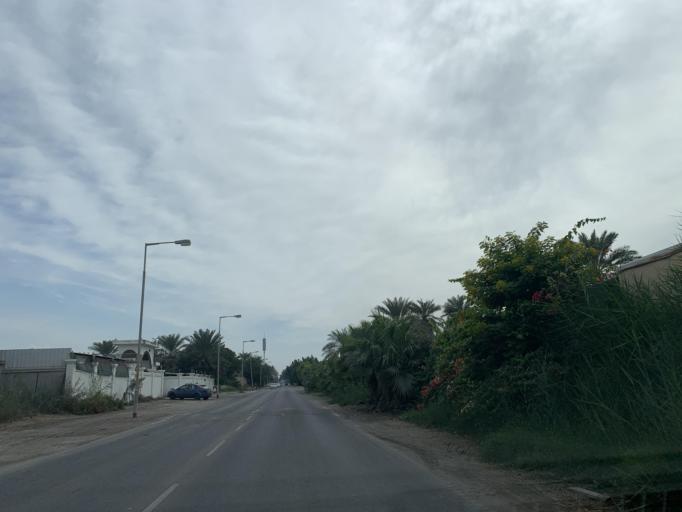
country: BH
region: Central Governorate
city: Madinat Hamad
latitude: 26.1266
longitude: 50.4709
